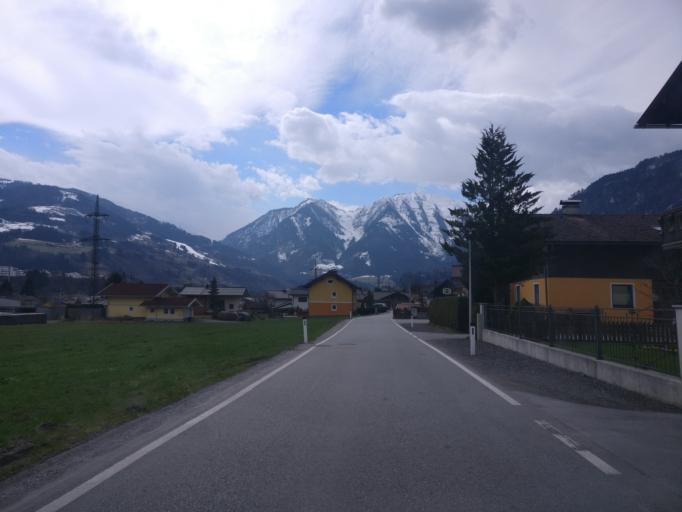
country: AT
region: Salzburg
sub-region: Politischer Bezirk Sankt Johann im Pongau
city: Sankt Johann im Pongau
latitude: 47.3567
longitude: 13.1954
